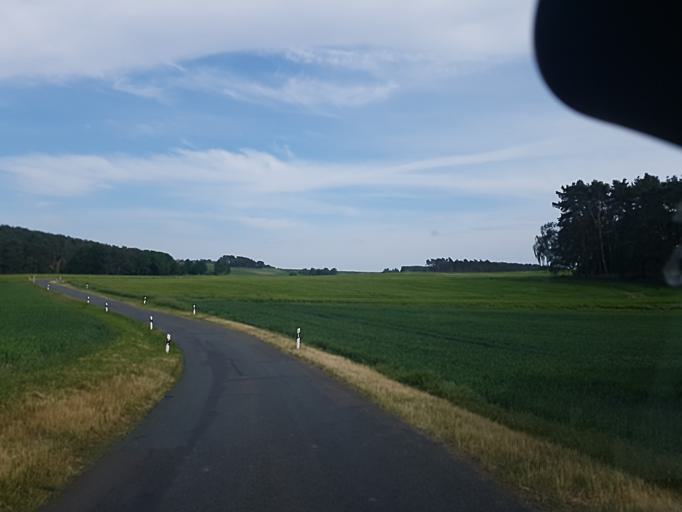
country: DE
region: Brandenburg
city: Niemegk
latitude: 52.0261
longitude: 12.6419
